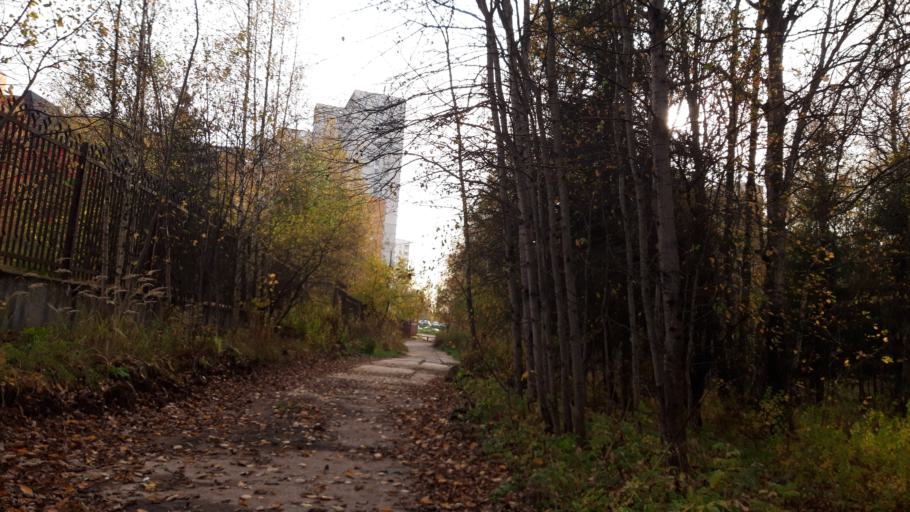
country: RU
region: Moscow
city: Zelenograd
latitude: 56.0013
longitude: 37.1924
